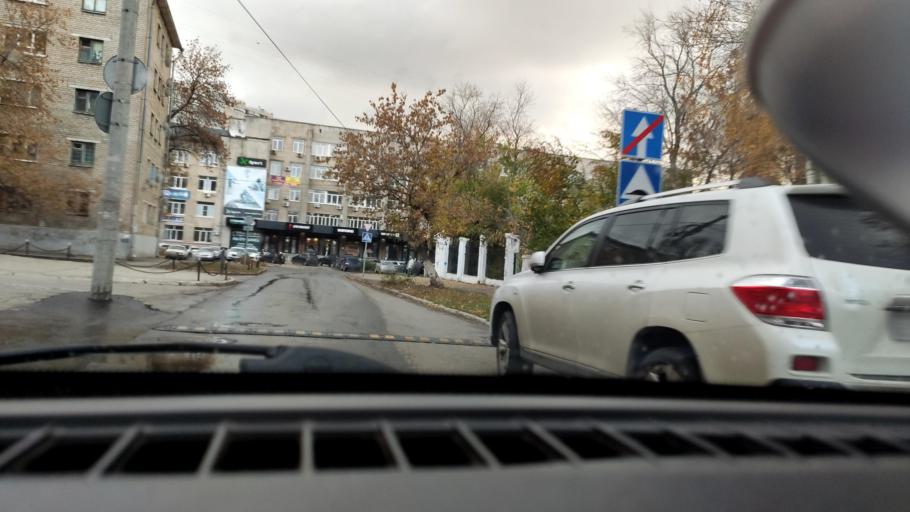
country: RU
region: Samara
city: Samara
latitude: 53.1951
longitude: 50.1319
